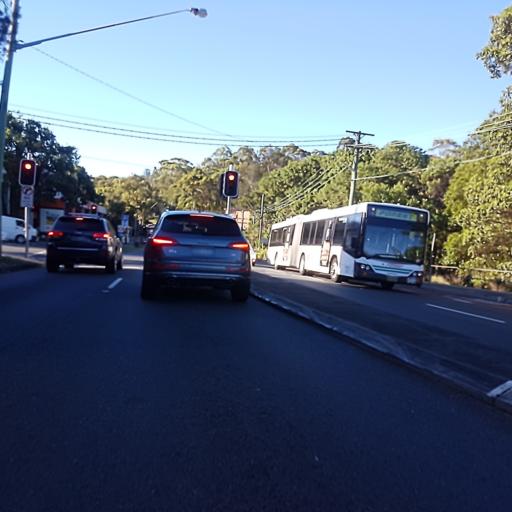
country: AU
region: New South Wales
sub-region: Willoughby
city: Castle Cove
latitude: -33.7860
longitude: 151.2012
